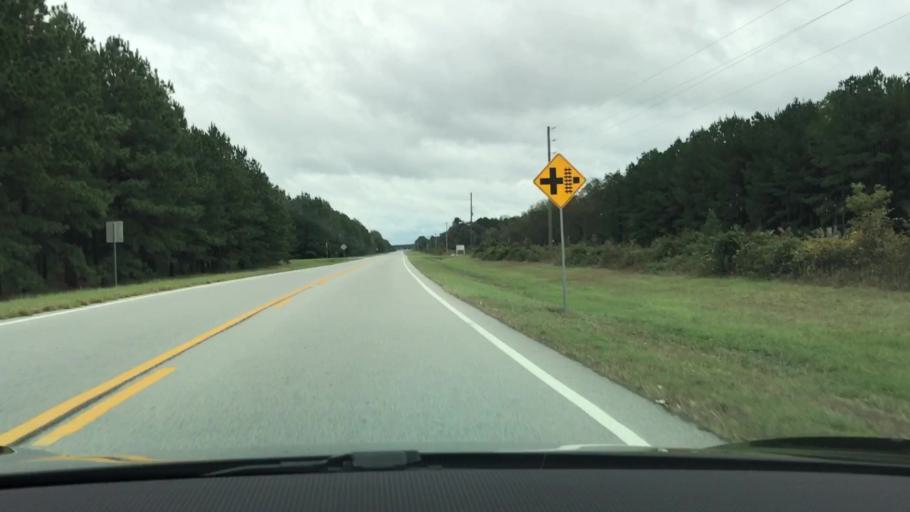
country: US
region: Georgia
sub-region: Glascock County
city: Gibson
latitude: 33.3042
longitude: -82.5235
